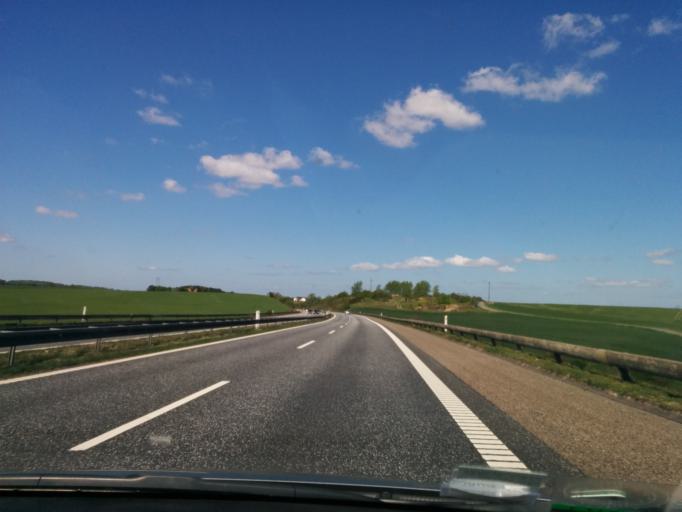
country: DK
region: Central Jutland
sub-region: Randers Kommune
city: Assentoft
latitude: 56.3788
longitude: 10.1162
